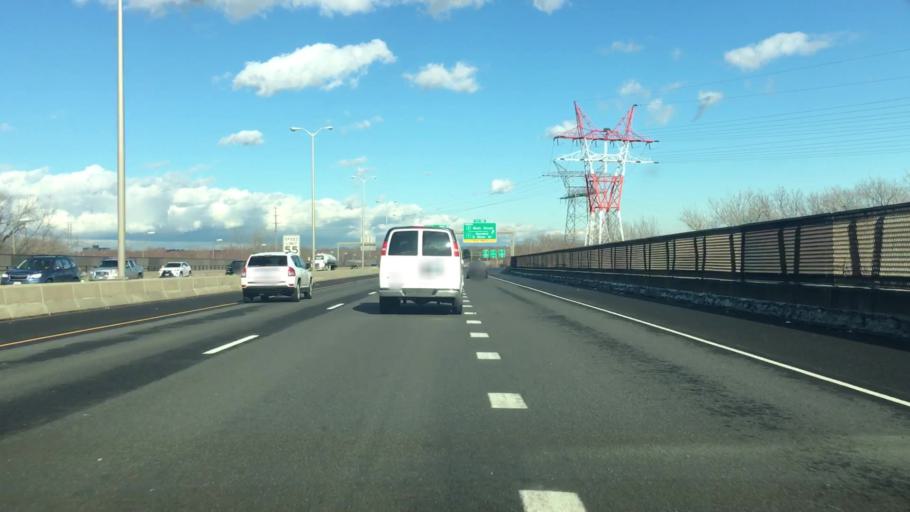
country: US
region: Connecticut
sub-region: Hartford County
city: Hartford
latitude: 41.7544
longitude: -72.6544
